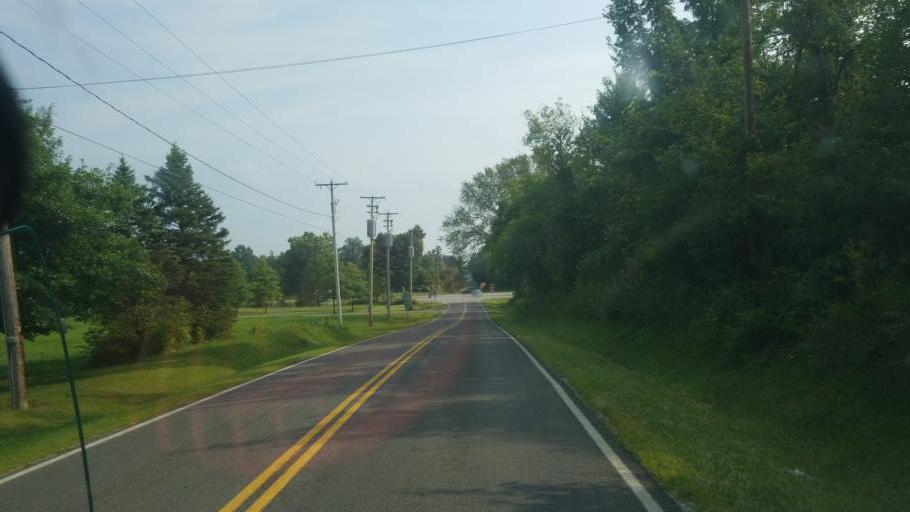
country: US
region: Ohio
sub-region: Medina County
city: Westfield Center
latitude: 41.0405
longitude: -81.9413
